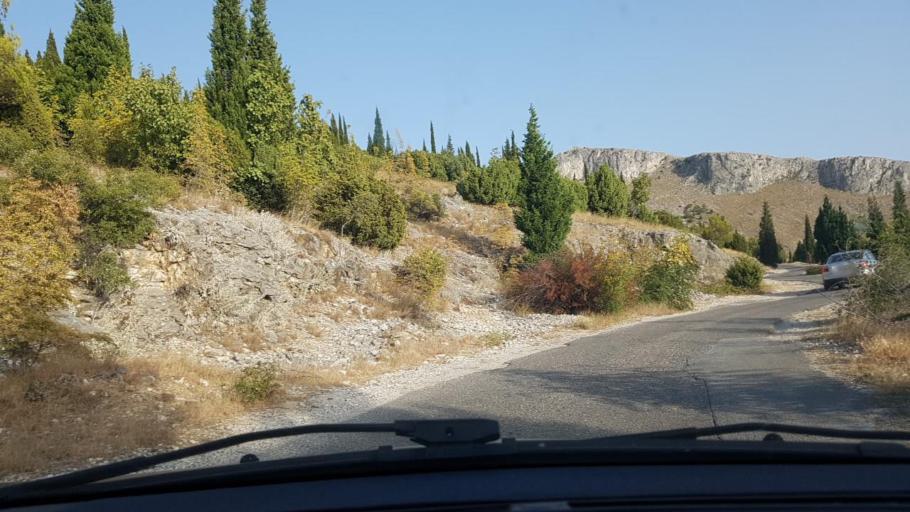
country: BA
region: Federation of Bosnia and Herzegovina
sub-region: Hercegovacko-Bosanski Kanton
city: Mostar
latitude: 43.3496
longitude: 17.8249
